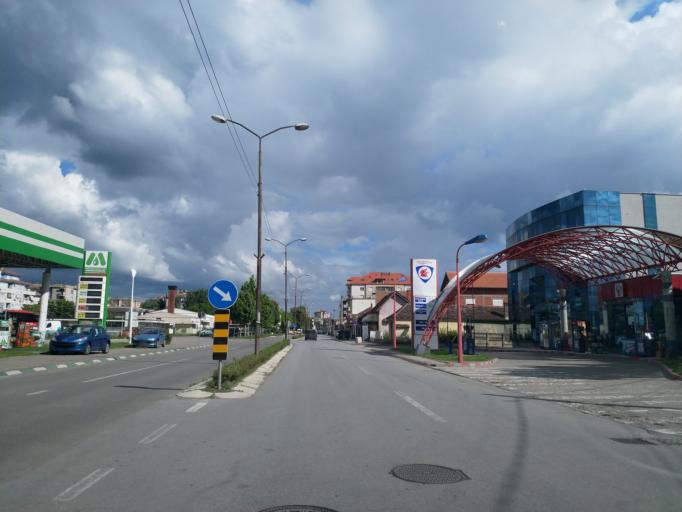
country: RS
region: Central Serbia
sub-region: Pomoravski Okrug
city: Paracin
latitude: 43.8673
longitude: 21.4055
